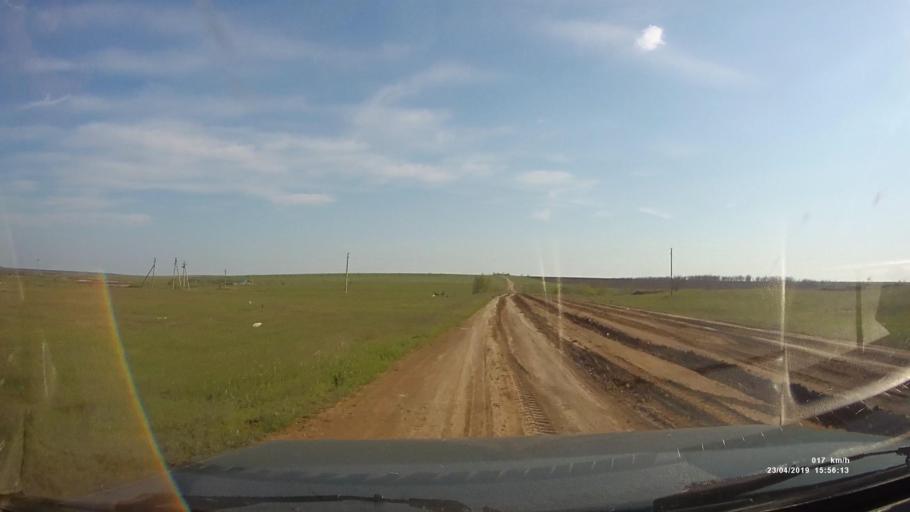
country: RU
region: Rostov
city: Remontnoye
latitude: 46.5380
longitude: 43.1114
